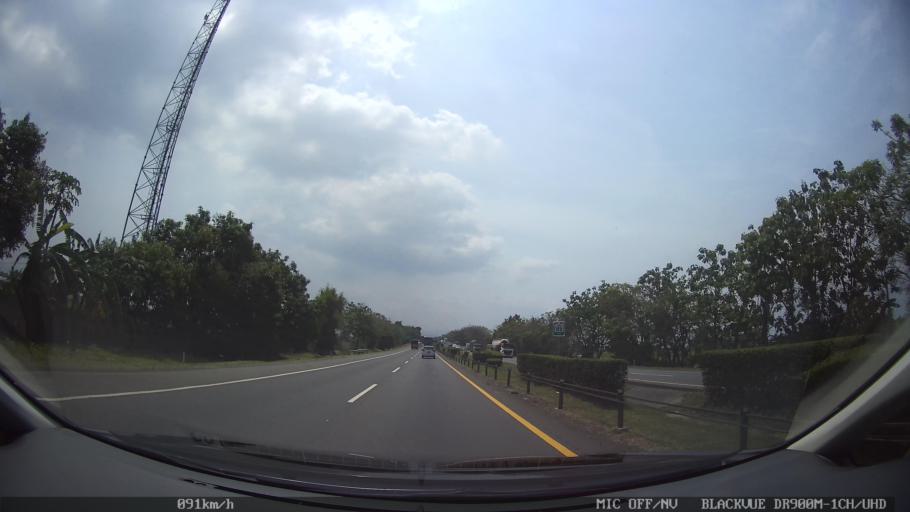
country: ID
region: Banten
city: Bojonegara
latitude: -6.0336
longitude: 106.1009
